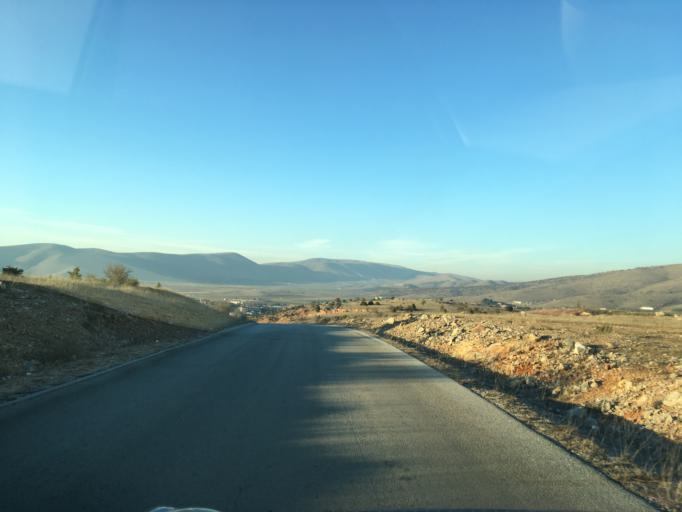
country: GR
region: West Macedonia
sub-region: Nomos Kozanis
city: Kozani
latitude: 40.2762
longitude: 21.7348
